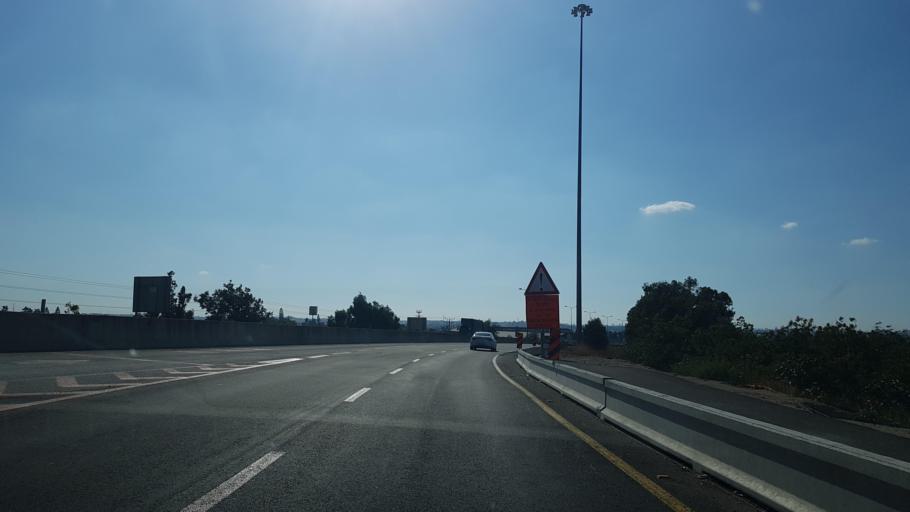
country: PS
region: West Bank
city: Tulkarm
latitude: 32.3125
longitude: 35.0084
